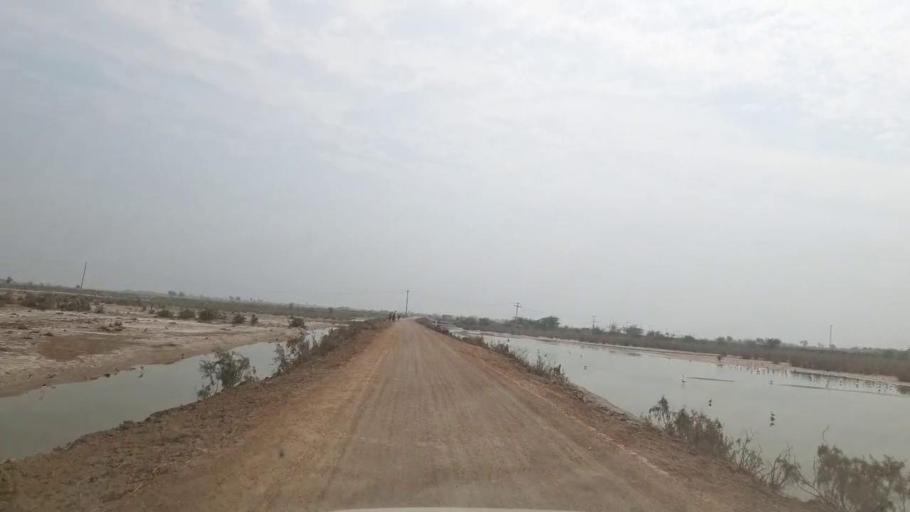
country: PK
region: Sindh
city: Mirpur Khas
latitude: 25.5536
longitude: 69.1226
